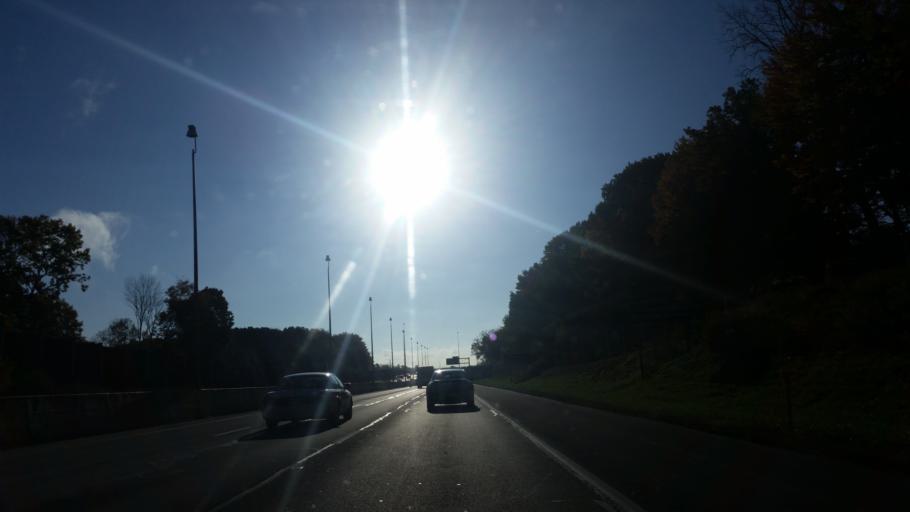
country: US
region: Ohio
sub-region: Summit County
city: Fairlawn
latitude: 41.1083
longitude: -81.6032
